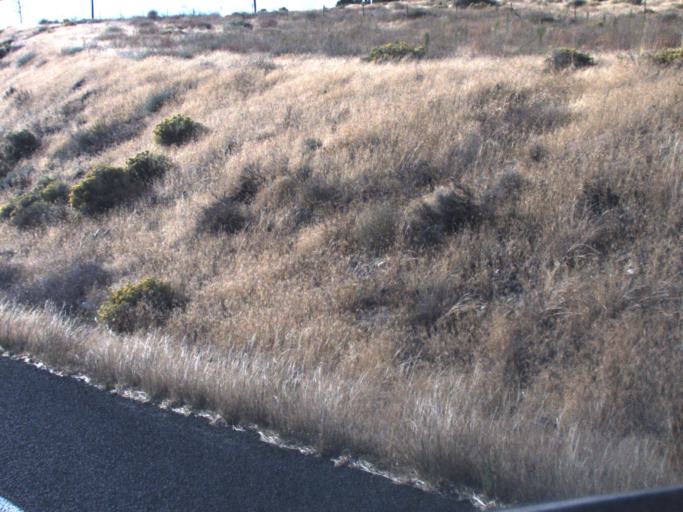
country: US
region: Oregon
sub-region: Morrow County
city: Boardman
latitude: 45.8686
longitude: -119.7679
